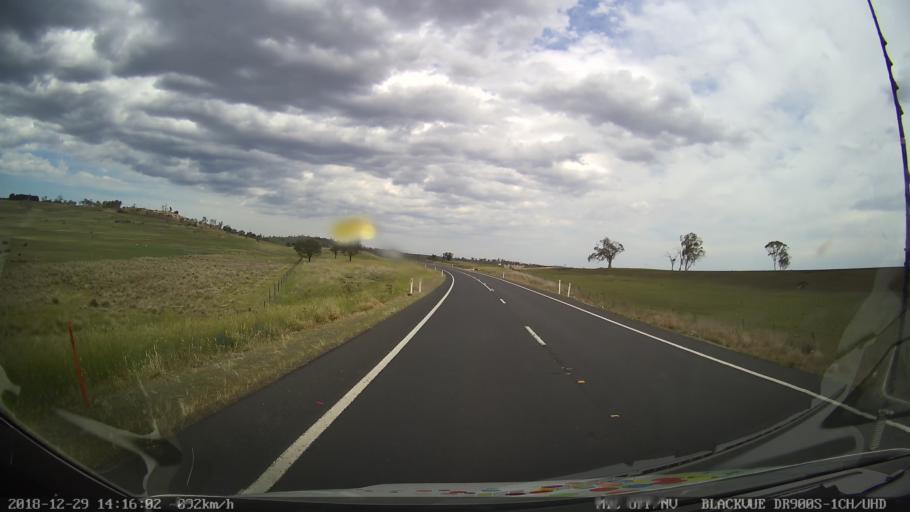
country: AU
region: New South Wales
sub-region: Cooma-Monaro
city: Cooma
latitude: -36.4629
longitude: 149.2457
